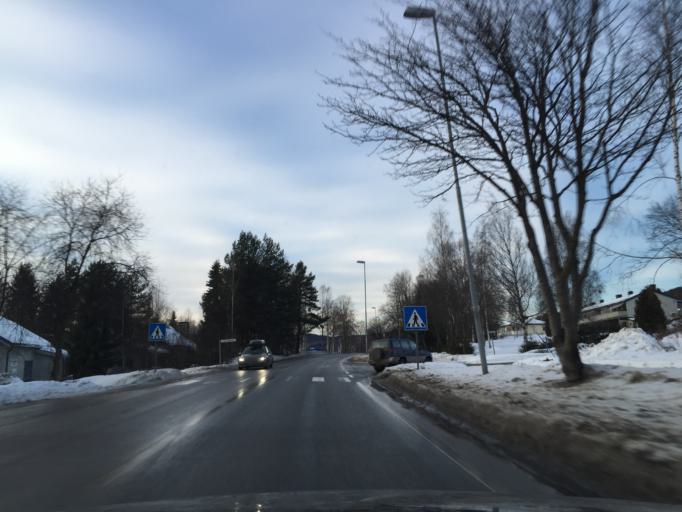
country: NO
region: Hedmark
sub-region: Kongsvinger
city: Kongsvinger
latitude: 60.1980
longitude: 11.9838
